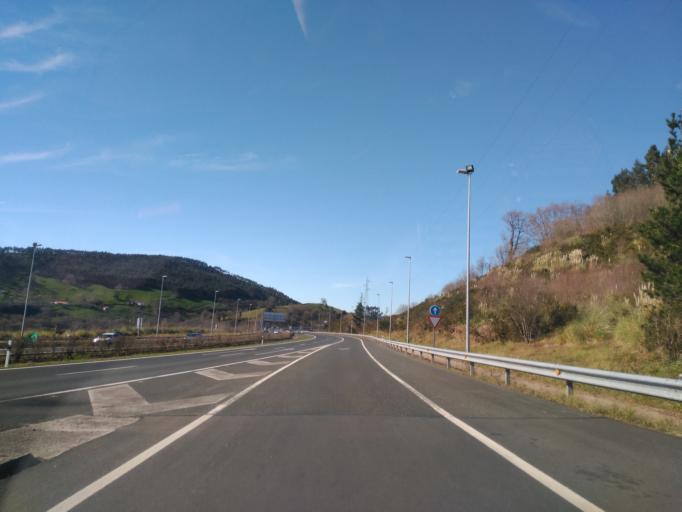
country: ES
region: Cantabria
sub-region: Provincia de Cantabria
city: Cabezon de la Sal
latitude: 43.3177
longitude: -4.2531
